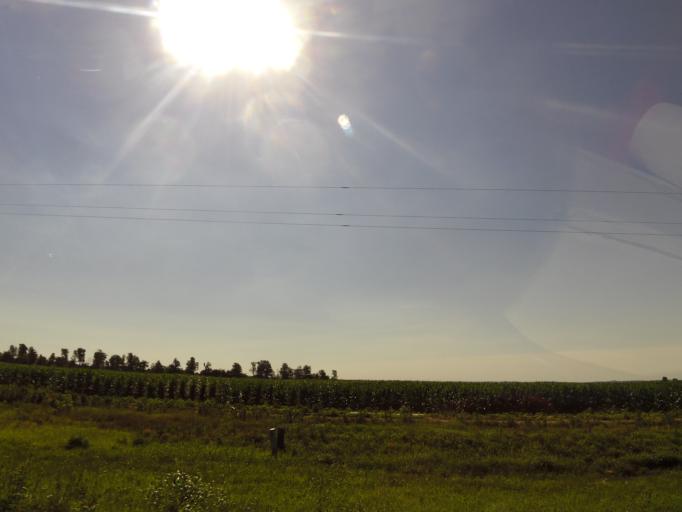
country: US
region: Arkansas
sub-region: Clay County
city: Corning
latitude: 36.4183
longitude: -90.4740
